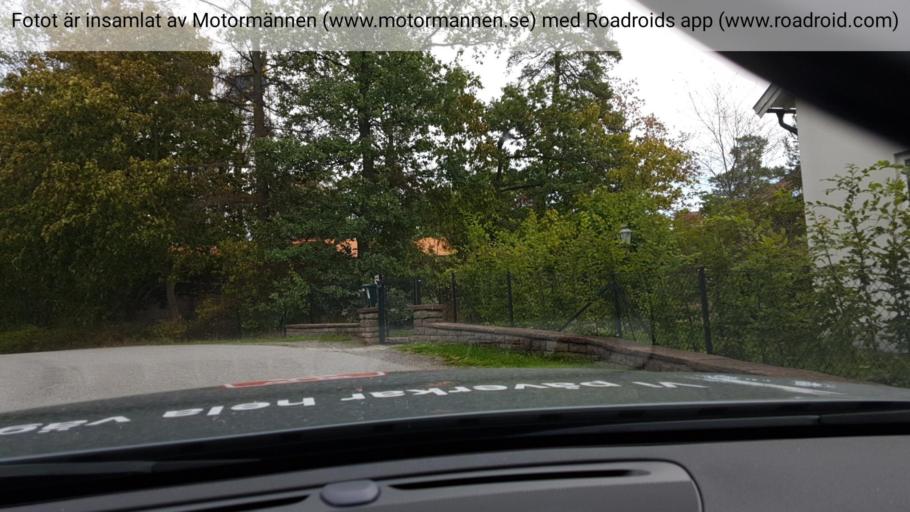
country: SE
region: Stockholm
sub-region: Danderyds Kommun
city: Djursholm
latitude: 59.3818
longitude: 18.0638
